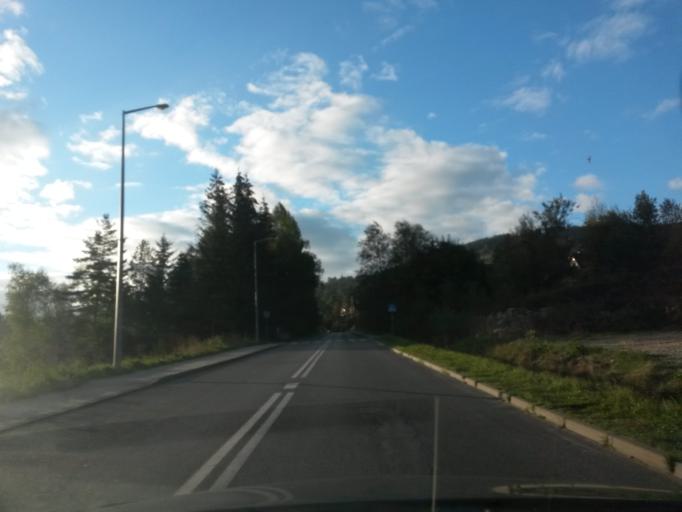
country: PL
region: Lesser Poland Voivodeship
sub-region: Powiat tatrzanski
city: Koscielisko
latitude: 49.2896
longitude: 19.9180
